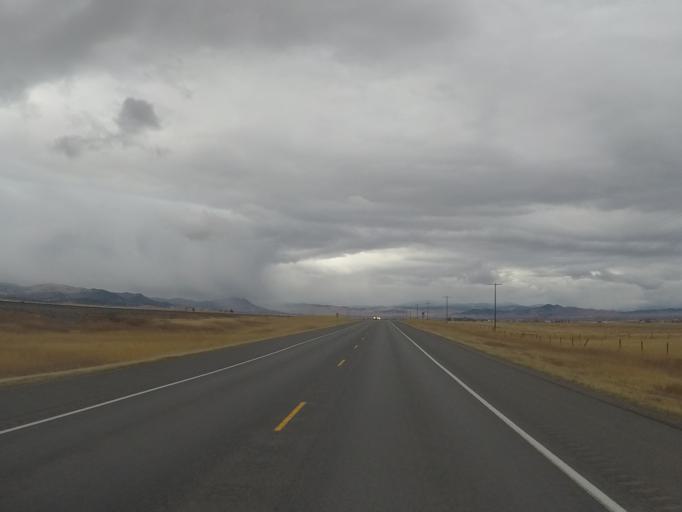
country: US
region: Montana
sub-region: Lewis and Clark County
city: East Helena
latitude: 46.5846
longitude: -111.8619
